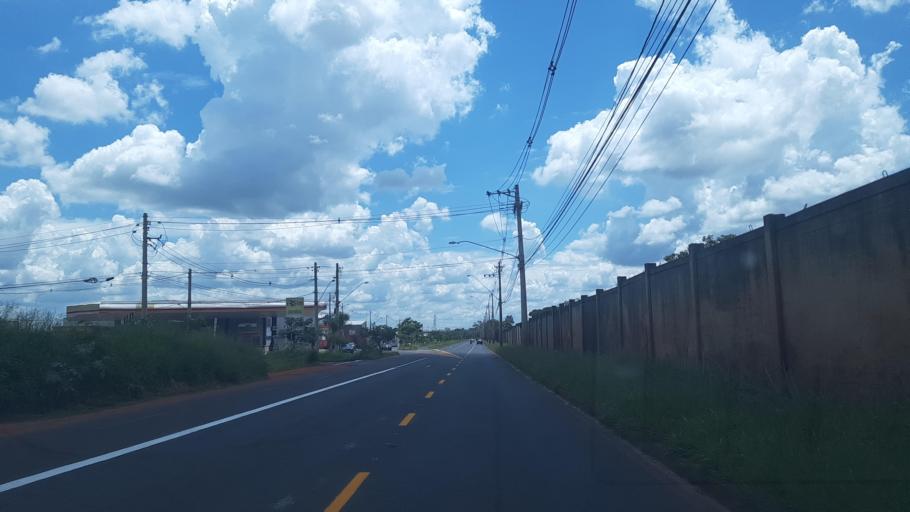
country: BR
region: Minas Gerais
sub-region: Uberlandia
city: Uberlandia
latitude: -18.9612
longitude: -48.3385
